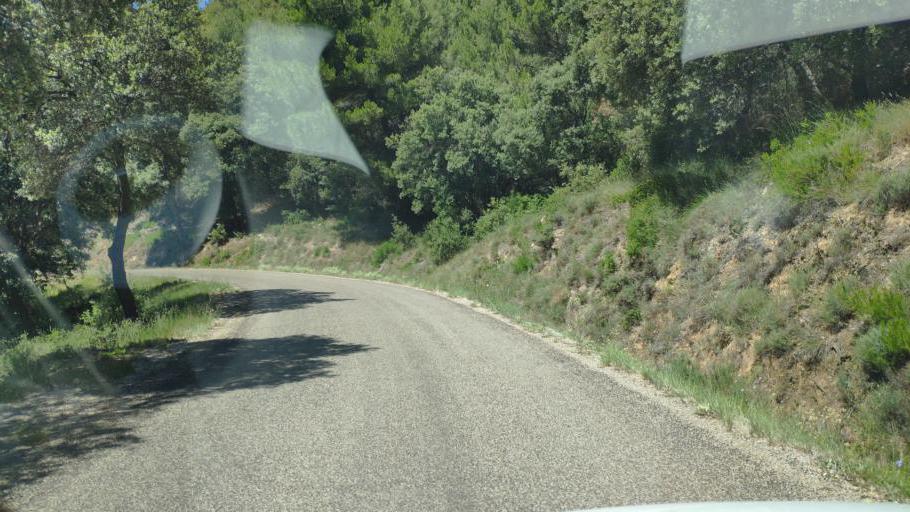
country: FR
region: Provence-Alpes-Cote d'Azur
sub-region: Departement du Vaucluse
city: Malaucene
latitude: 44.1811
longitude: 5.0917
